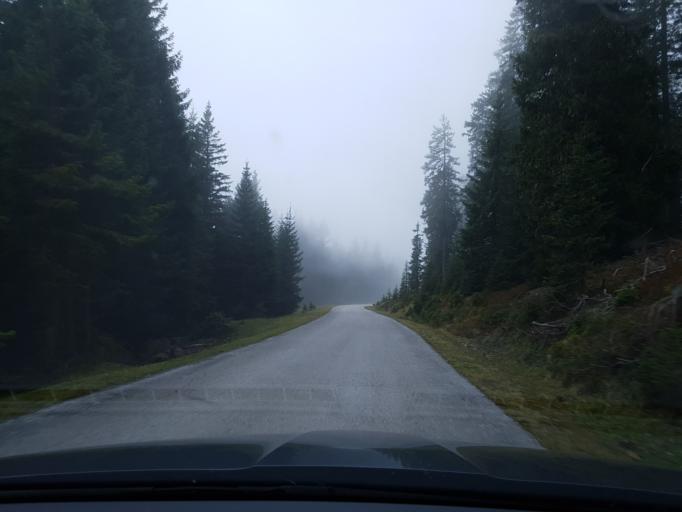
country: AT
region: Salzburg
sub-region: Politischer Bezirk Sankt Johann im Pongau
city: Filzmoos
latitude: 47.4109
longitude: 13.4852
